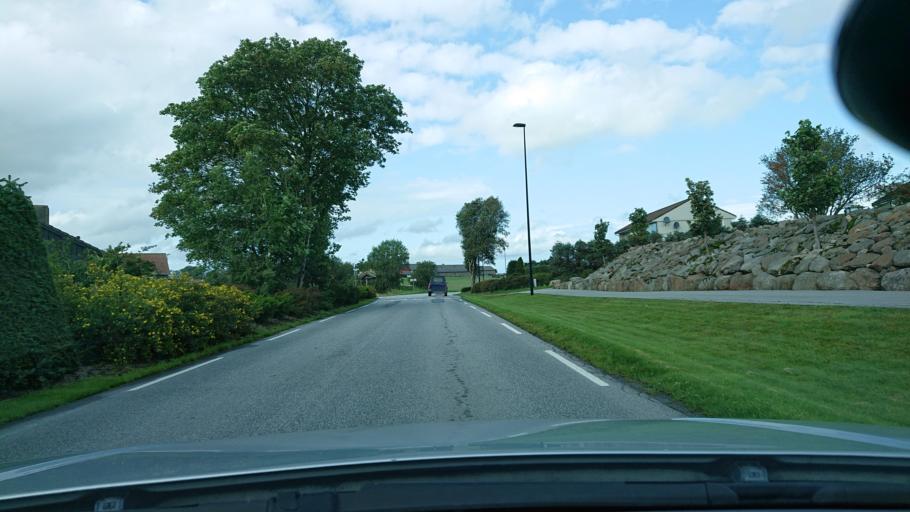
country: NO
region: Rogaland
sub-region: Gjesdal
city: Algard
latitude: 58.6875
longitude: 5.7678
